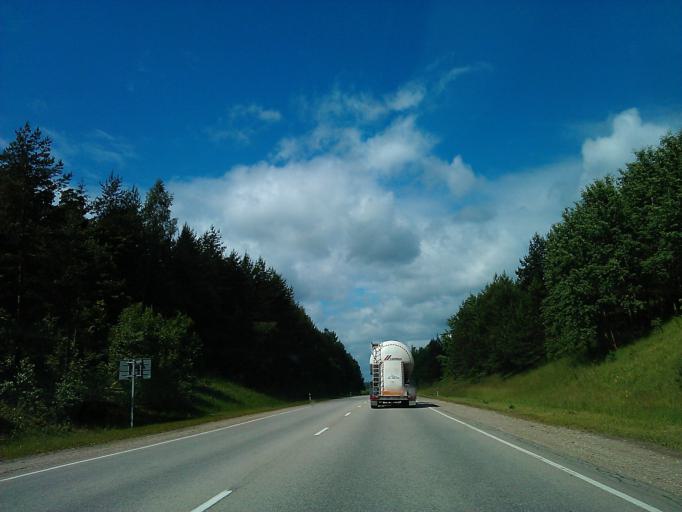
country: LV
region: Tukuma Rajons
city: Tukums
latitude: 56.9465
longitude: 23.1358
